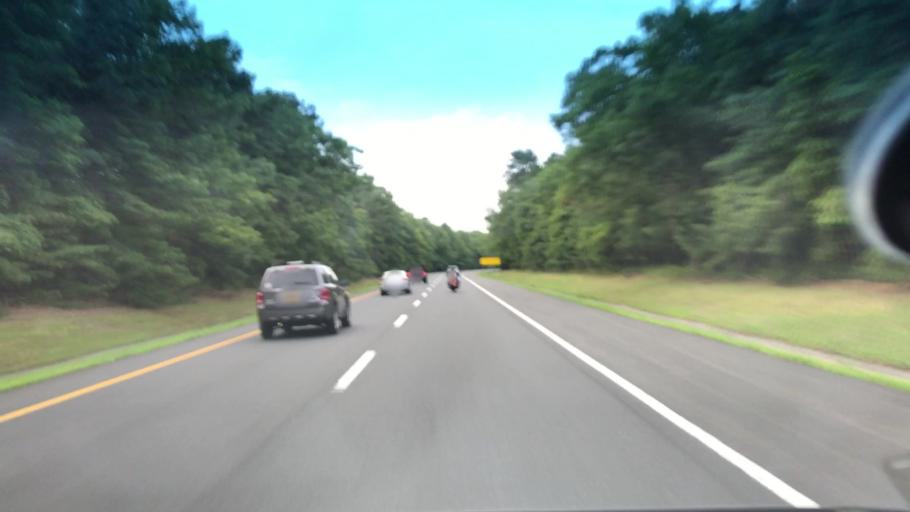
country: US
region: New York
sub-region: Suffolk County
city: East Shoreham
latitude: 40.9398
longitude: -72.8778
